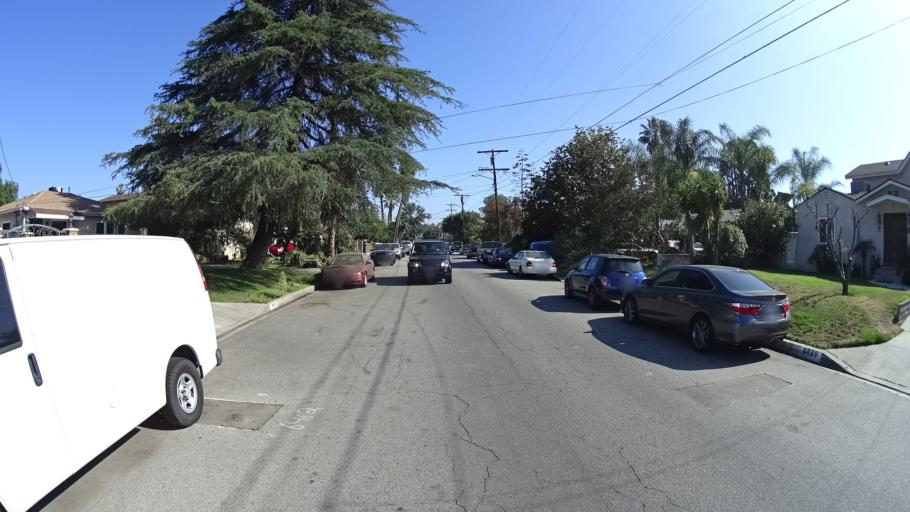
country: US
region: California
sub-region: Los Angeles County
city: Van Nuys
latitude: 34.1884
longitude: -118.4247
